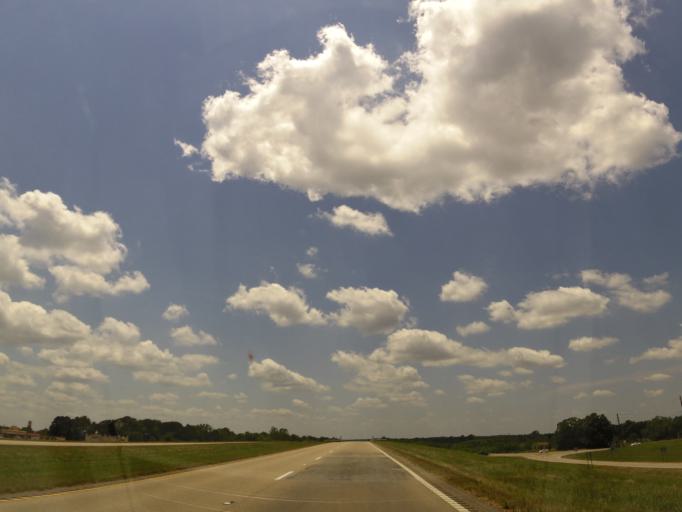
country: US
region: Mississippi
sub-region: Pontotoc County
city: Pontotoc
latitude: 34.2873
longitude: -89.0237
